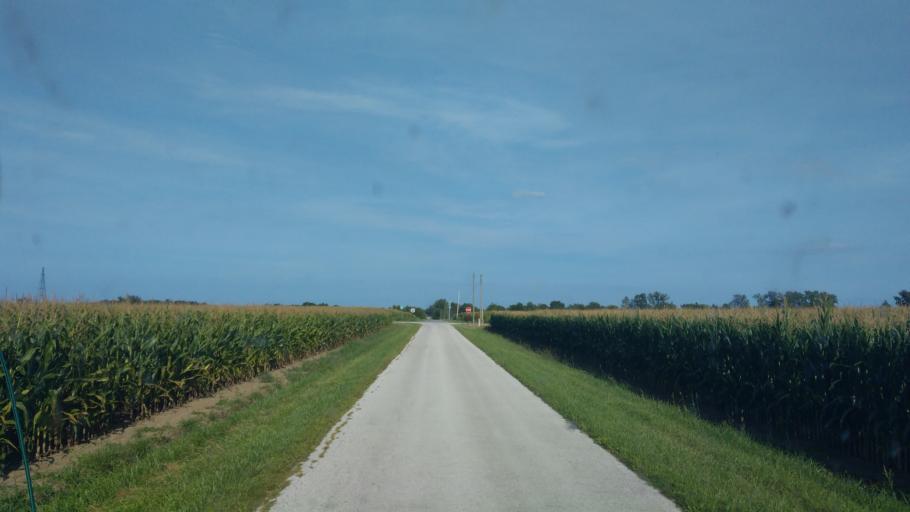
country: US
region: Ohio
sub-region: Wyandot County
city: Carey
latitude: 40.8466
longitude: -83.4009
